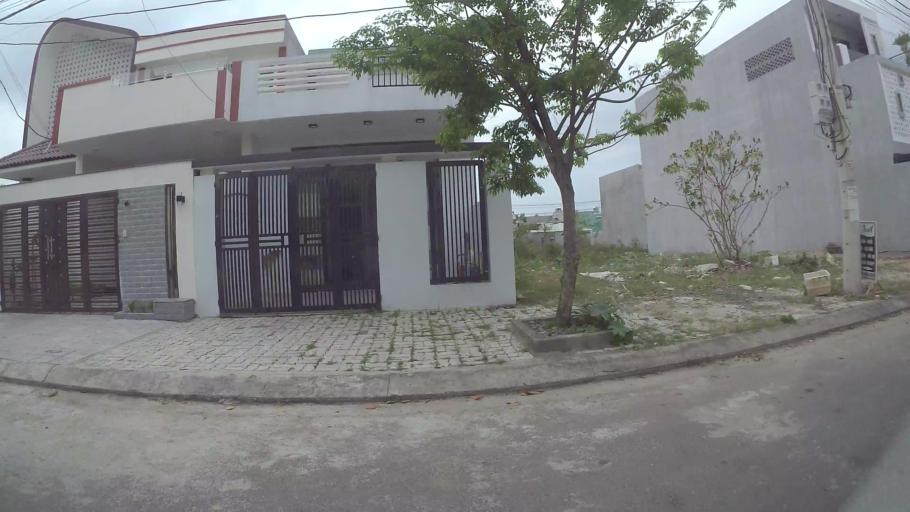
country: VN
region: Da Nang
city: Lien Chieu
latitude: 16.0439
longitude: 108.1679
